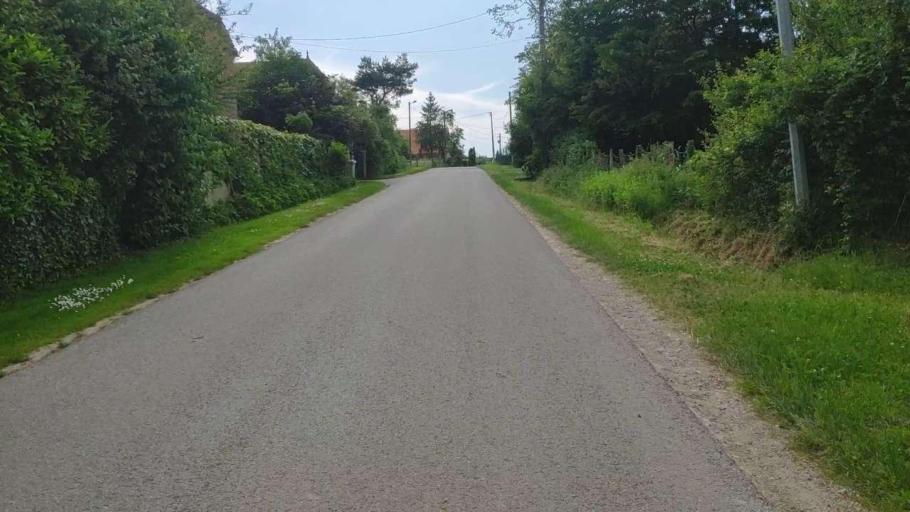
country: FR
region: Bourgogne
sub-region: Departement de Saone-et-Loire
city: Saint-Germain-du-Bois
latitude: 46.8014
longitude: 5.3333
